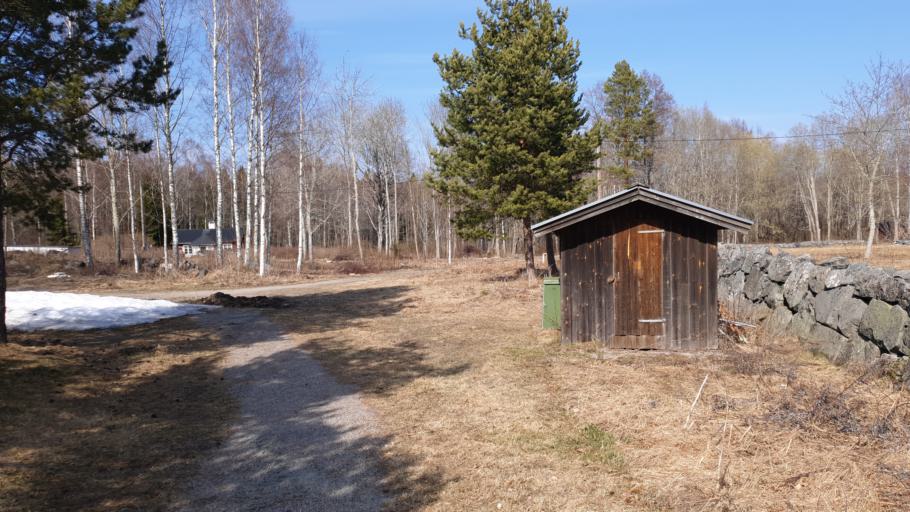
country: SE
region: Gaevleborg
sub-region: Gavle Kommun
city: Norrsundet
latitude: 61.0468
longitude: 17.1398
